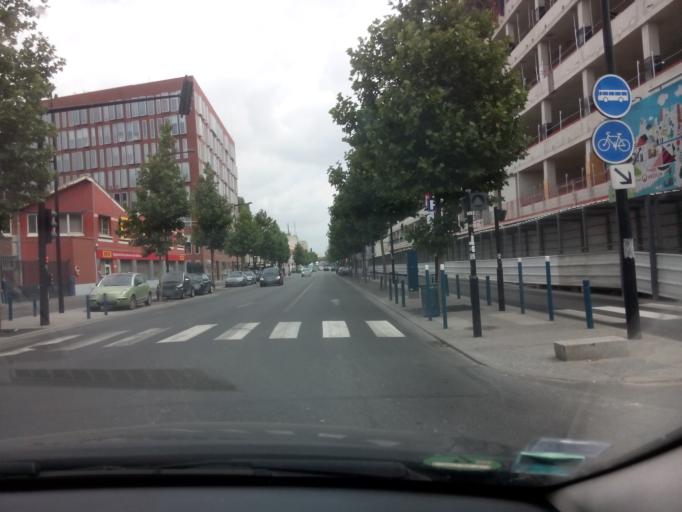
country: FR
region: Ile-de-France
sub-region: Departement de Seine-Saint-Denis
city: Aubervilliers
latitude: 48.9024
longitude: 2.3712
